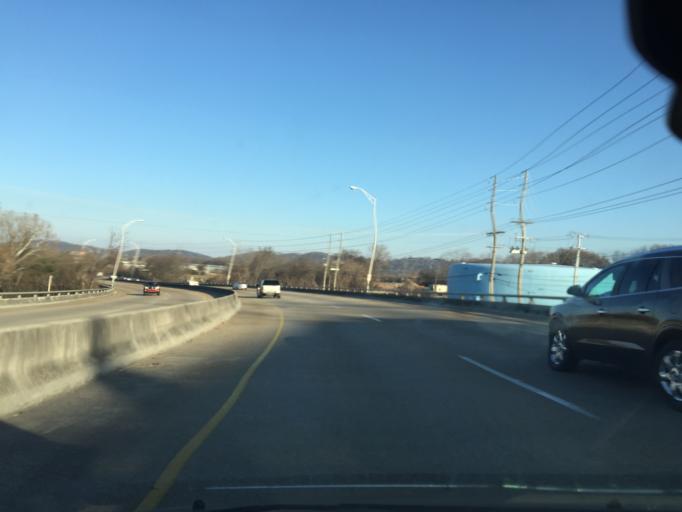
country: US
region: Tennessee
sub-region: Hamilton County
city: Chattanooga
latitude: 35.0523
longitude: -85.2892
